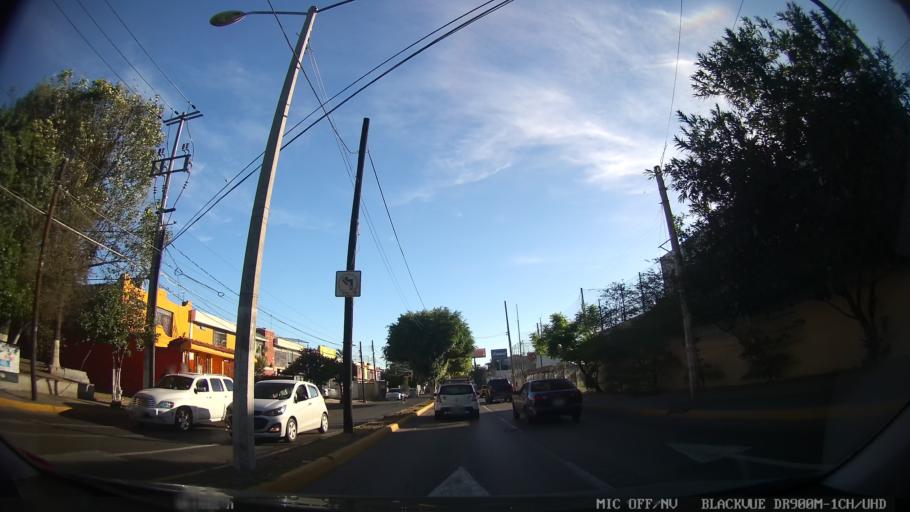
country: MX
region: Jalisco
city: Tlaquepaque
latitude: 20.6303
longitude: -103.3192
